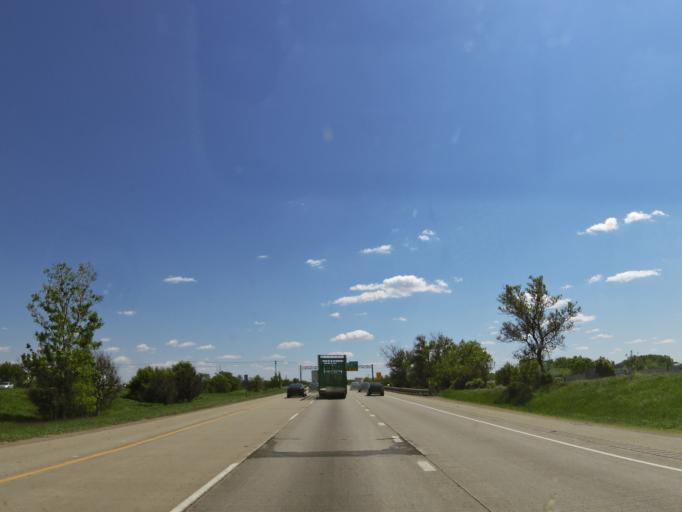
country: US
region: Wisconsin
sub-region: Dane County
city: McFarland
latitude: 43.0536
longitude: -89.2775
